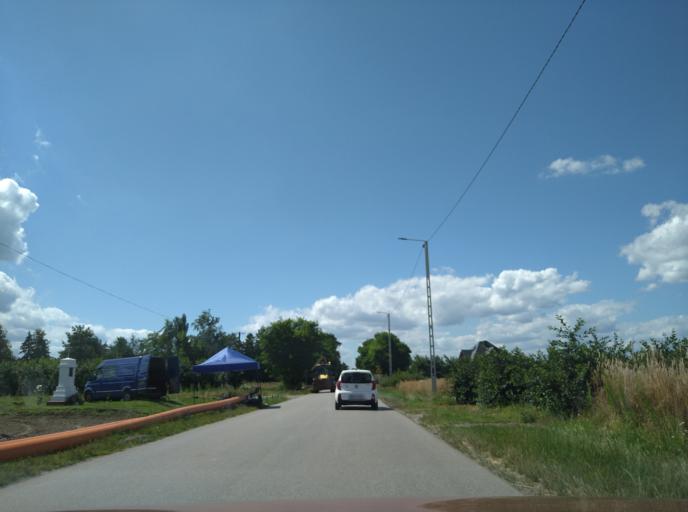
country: PL
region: Masovian Voivodeship
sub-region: Powiat bialobrzeski
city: Bialobrzegi
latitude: 51.6709
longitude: 20.9076
